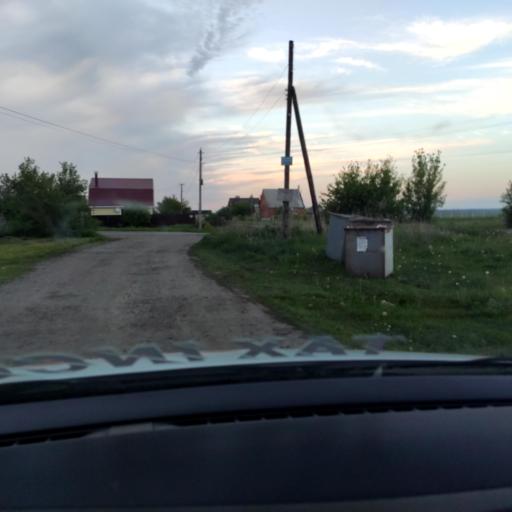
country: RU
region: Voronezj
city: Maslovka
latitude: 51.4560
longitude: 39.2382
